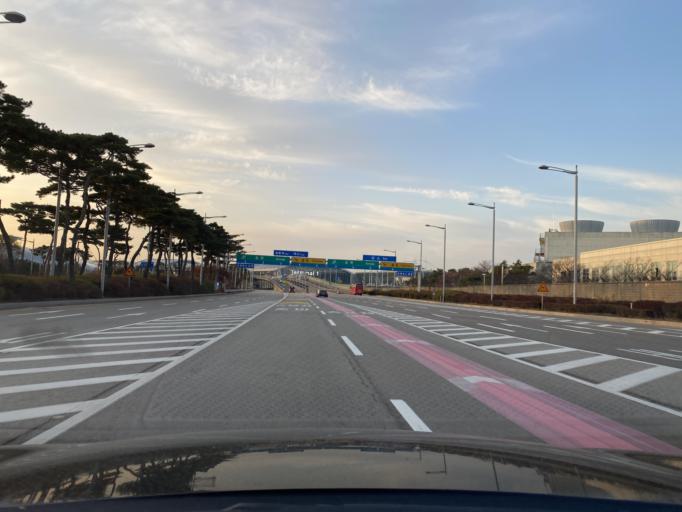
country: KR
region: Incheon
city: Incheon
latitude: 37.4474
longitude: 126.4604
